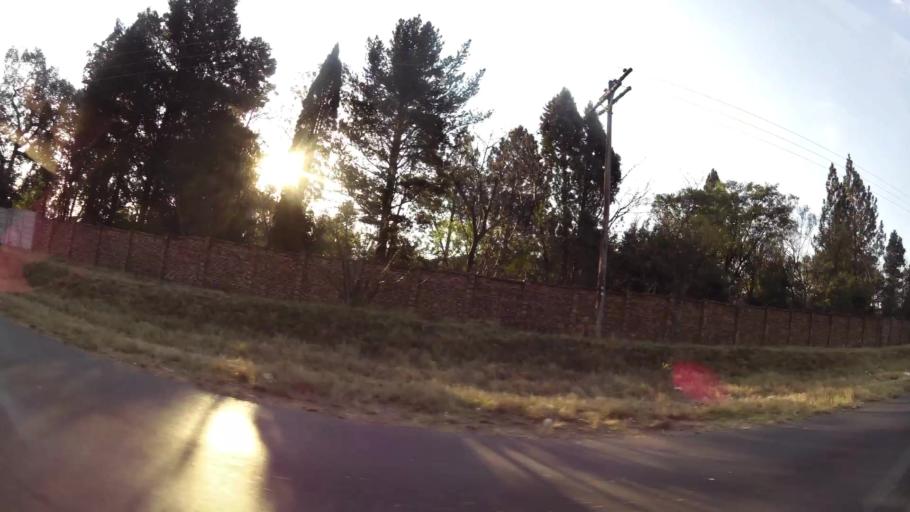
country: ZA
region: Gauteng
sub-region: City of Johannesburg Metropolitan Municipality
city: Midrand
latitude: -26.0281
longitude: 28.1450
